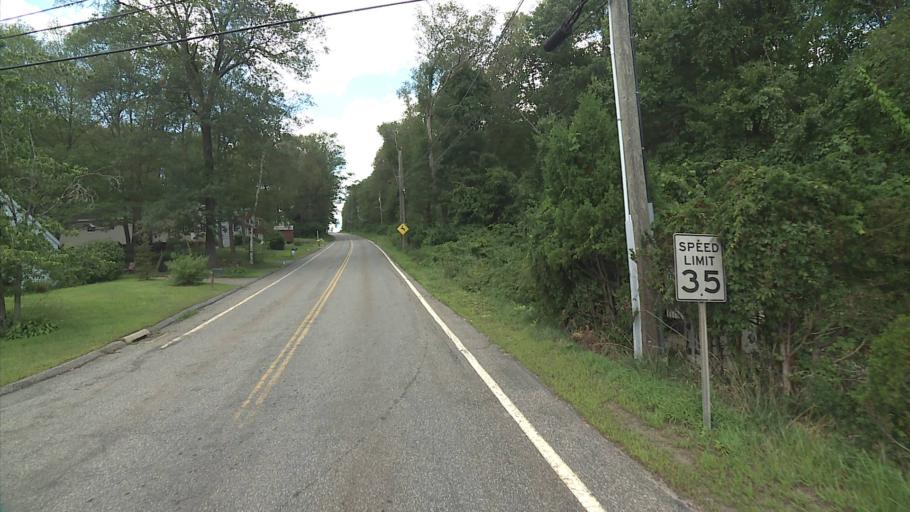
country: US
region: Connecticut
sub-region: Tolland County
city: Stafford
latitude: 41.9410
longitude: -72.1918
